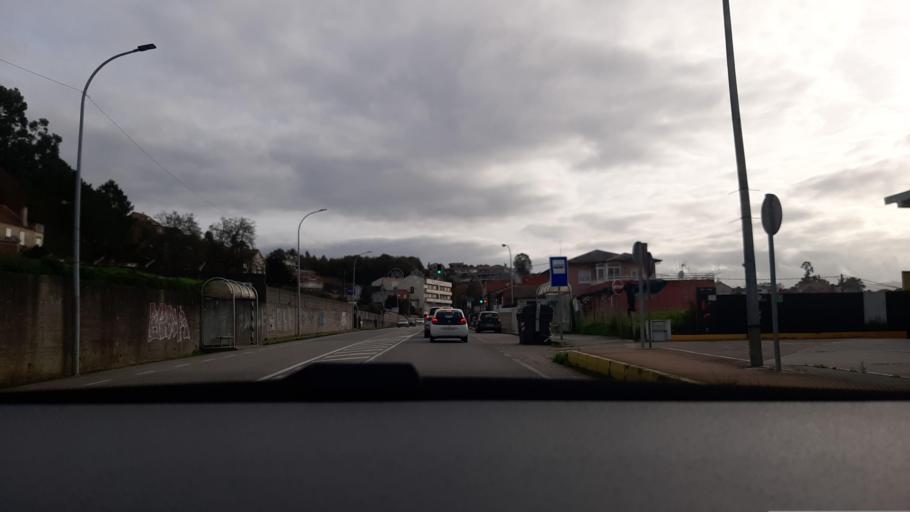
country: ES
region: Galicia
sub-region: Provincia de Pontevedra
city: Nigran
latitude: 42.1623
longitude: -8.8015
